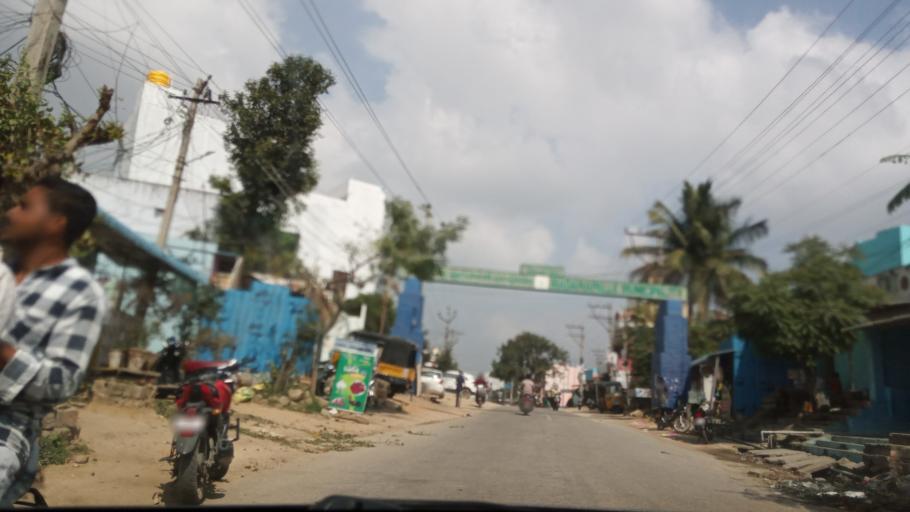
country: IN
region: Andhra Pradesh
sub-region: Chittoor
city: Madanapalle
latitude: 13.5666
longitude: 78.5136
